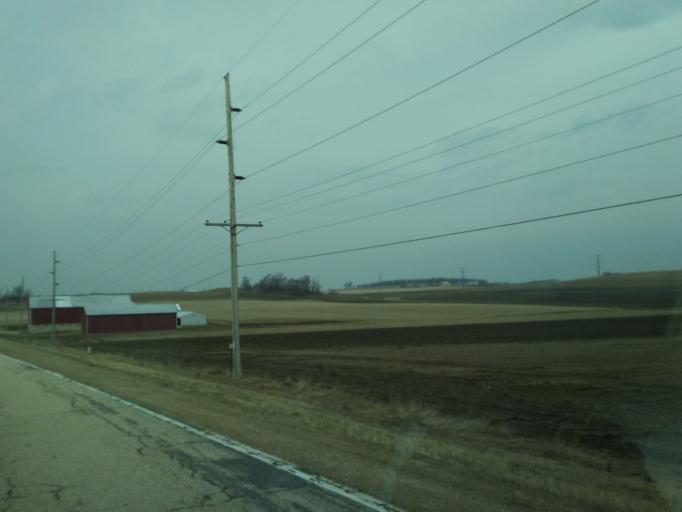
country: US
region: Wisconsin
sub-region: Dane County
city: Waunakee
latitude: 43.2503
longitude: -89.4622
